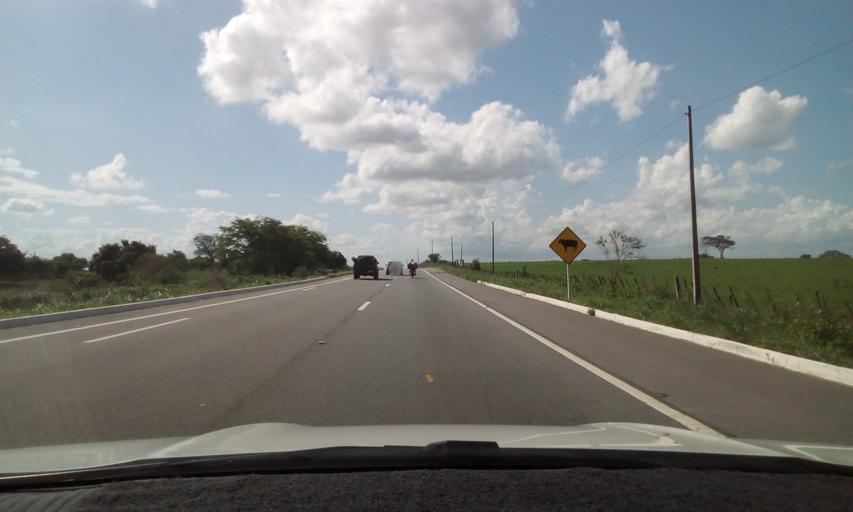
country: BR
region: Paraiba
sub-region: Pilar
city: Pilar
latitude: -7.1771
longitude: -35.3240
